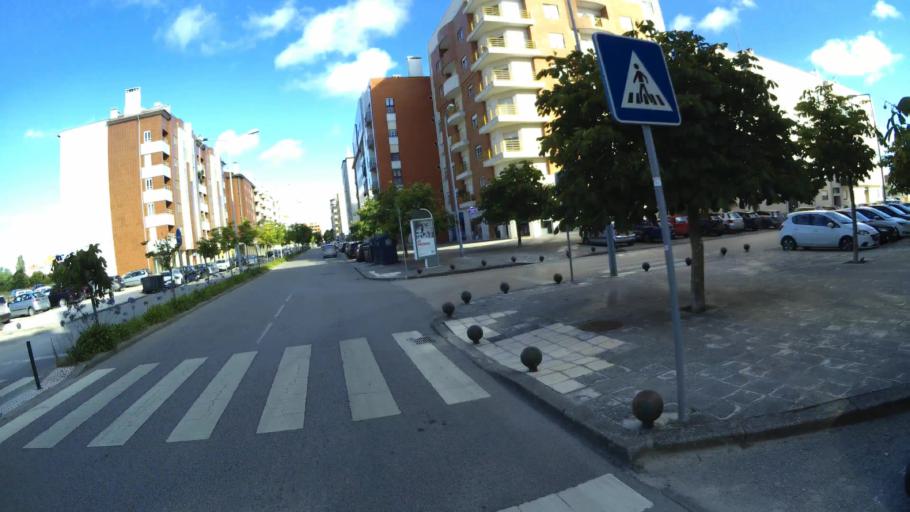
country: PT
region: Aveiro
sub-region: Aveiro
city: Aveiro
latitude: 40.6473
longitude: -8.6459
